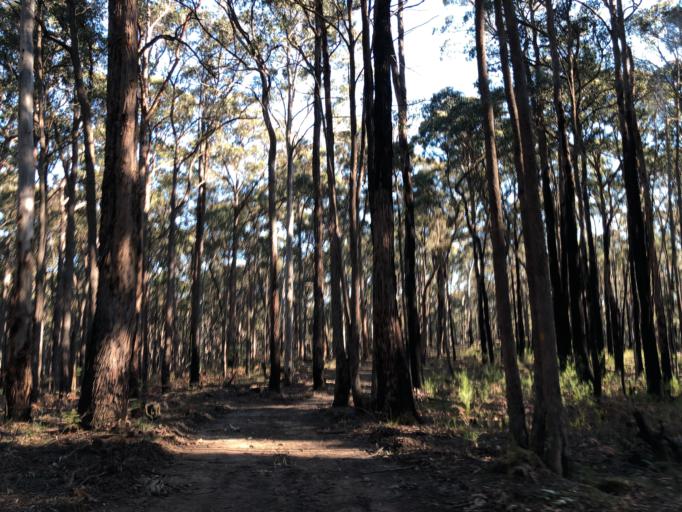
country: AU
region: Victoria
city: Brown Hill
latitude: -37.5099
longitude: 144.1823
